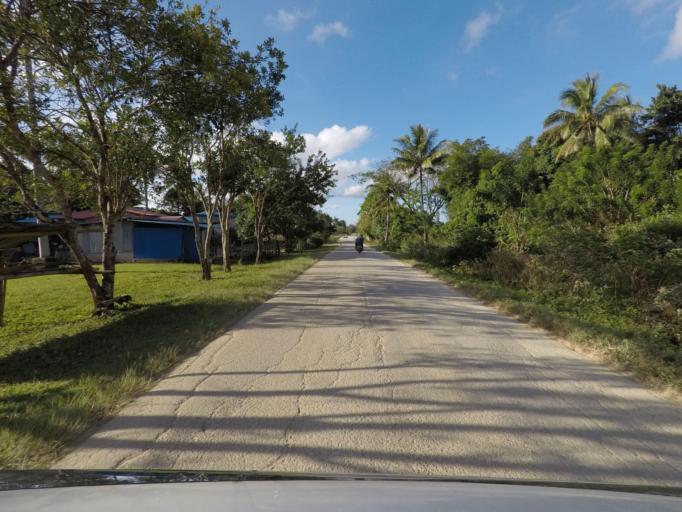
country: TL
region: Lautem
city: Lospalos
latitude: -8.4663
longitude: 126.9949
